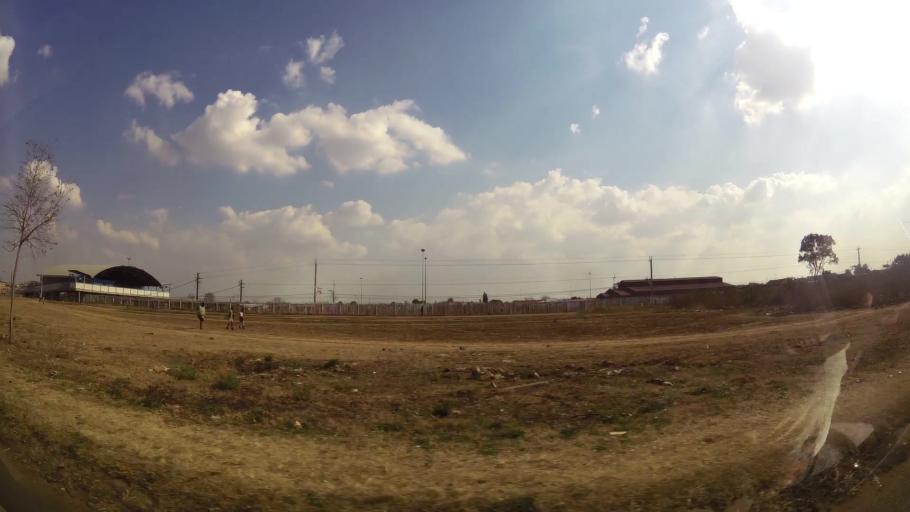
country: ZA
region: Gauteng
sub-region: Ekurhuleni Metropolitan Municipality
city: Germiston
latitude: -26.3398
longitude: 28.1533
